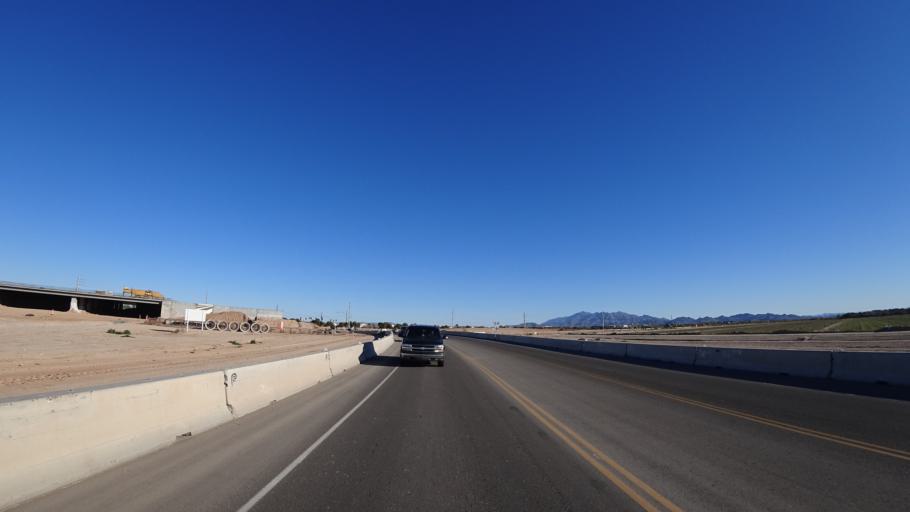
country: US
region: Arizona
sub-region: Maricopa County
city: Goodyear
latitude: 33.4498
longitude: -112.4287
